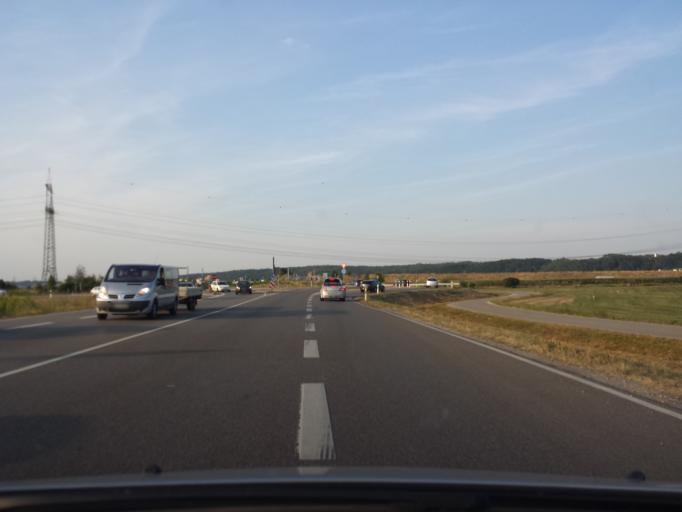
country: DE
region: Bavaria
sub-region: Swabia
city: Friedberg
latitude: 48.4008
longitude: 10.9520
